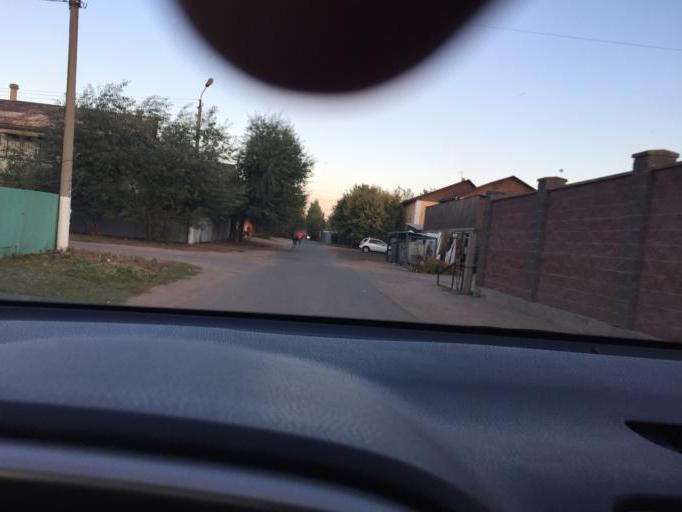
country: KZ
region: Astana Qalasy
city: Astana
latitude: 51.1423
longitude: 71.4213
